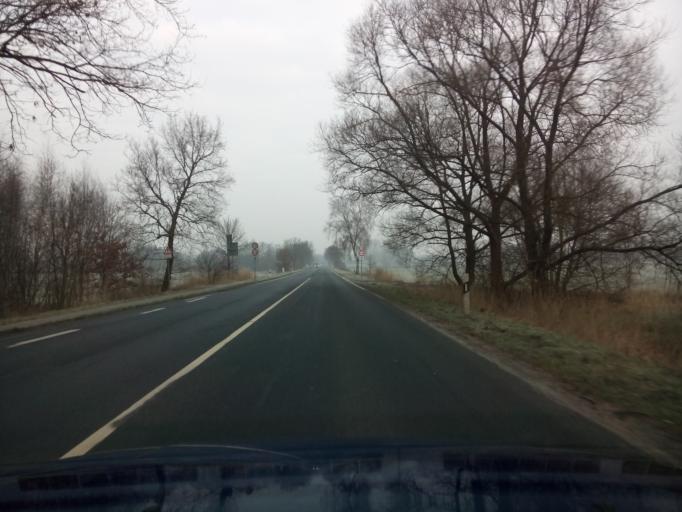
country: DE
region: Lower Saxony
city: Loxstedt
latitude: 53.4479
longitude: 8.6131
